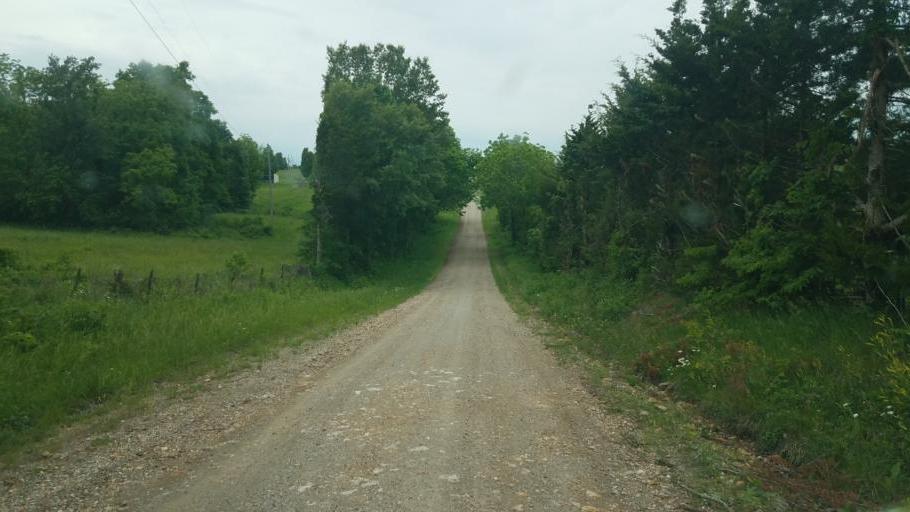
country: US
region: Missouri
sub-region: Moniteau County
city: California
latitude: 38.7107
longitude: -92.6377
